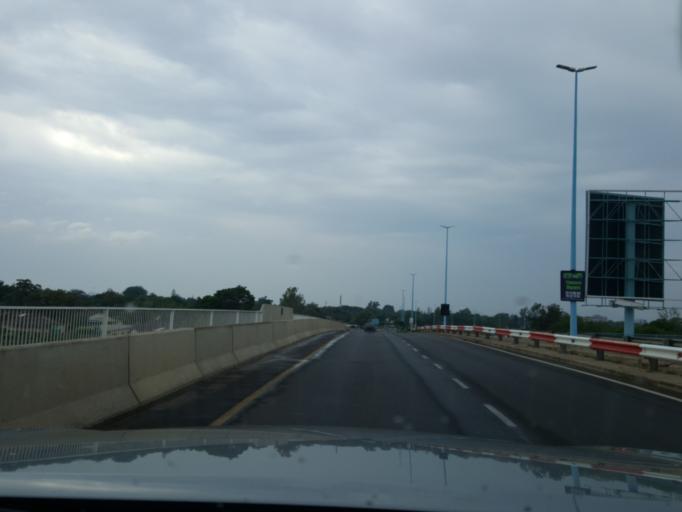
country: BW
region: South East
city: Gaborone
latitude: -24.6138
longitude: 25.9279
